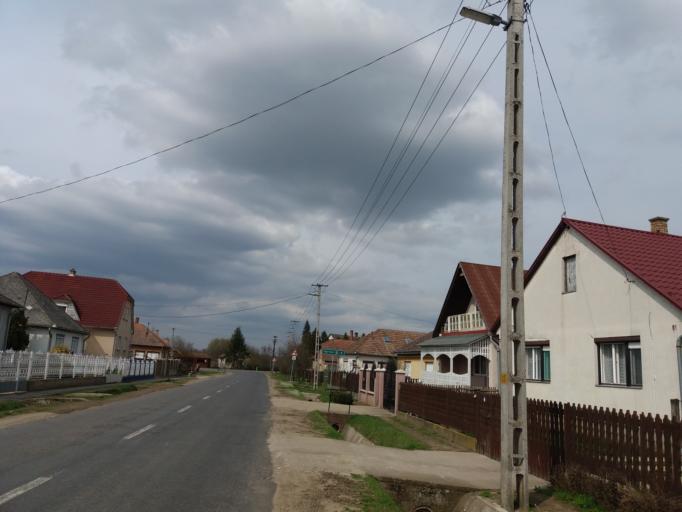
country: HU
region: Szabolcs-Szatmar-Bereg
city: Petnehaza
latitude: 48.0587
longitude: 22.0435
